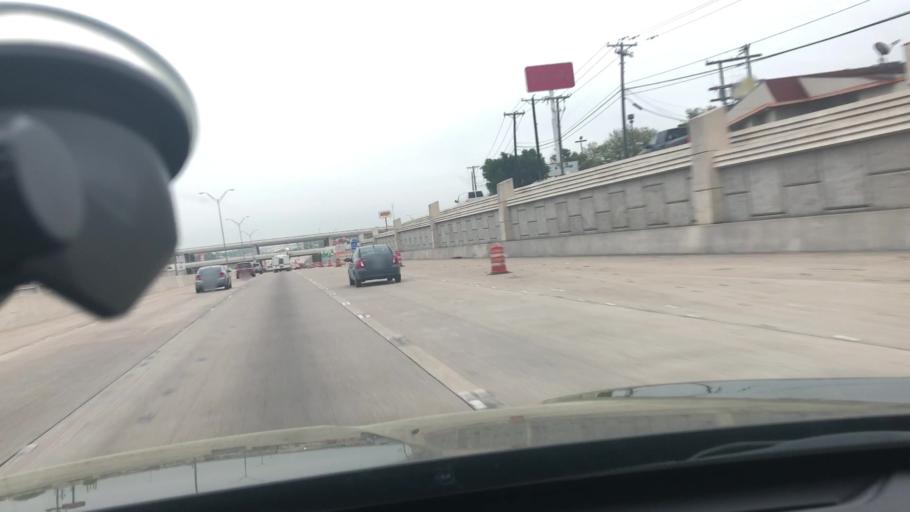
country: US
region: Texas
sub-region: Bell County
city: Temple
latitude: 31.0893
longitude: -97.3910
